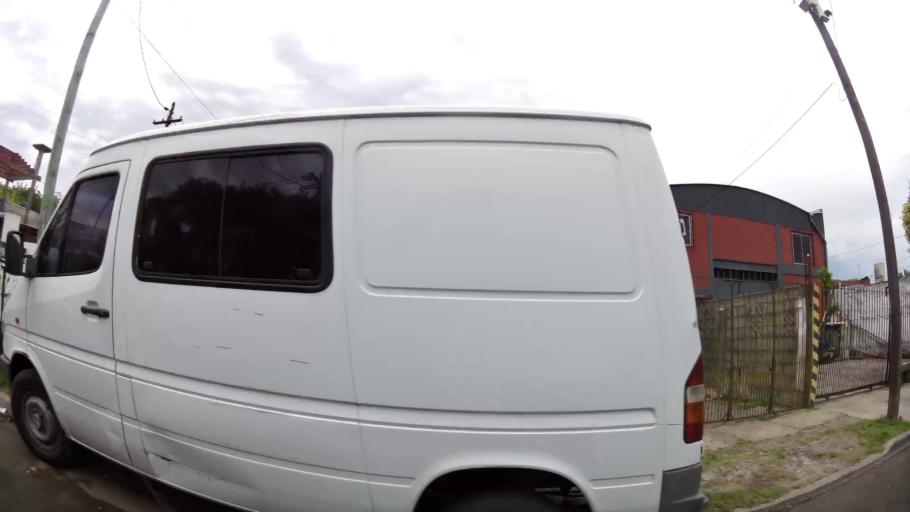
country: AR
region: Buenos Aires
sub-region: Partido de Quilmes
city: Quilmes
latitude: -34.7534
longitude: -58.2065
